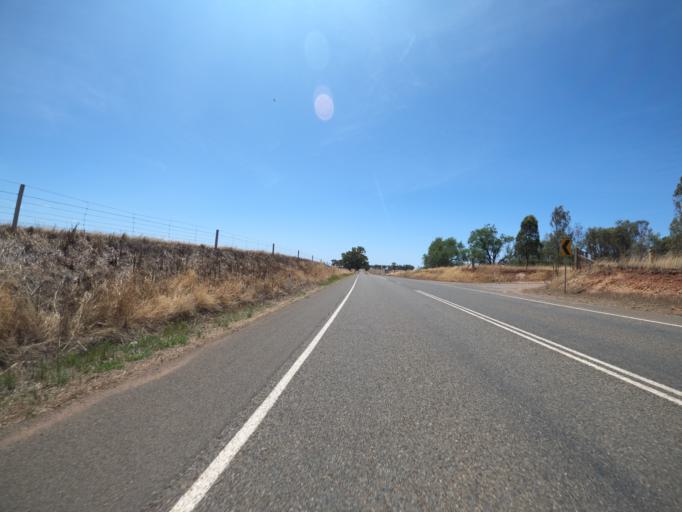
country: AU
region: Victoria
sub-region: Moira
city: Yarrawonga
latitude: -36.0975
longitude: 145.9954
